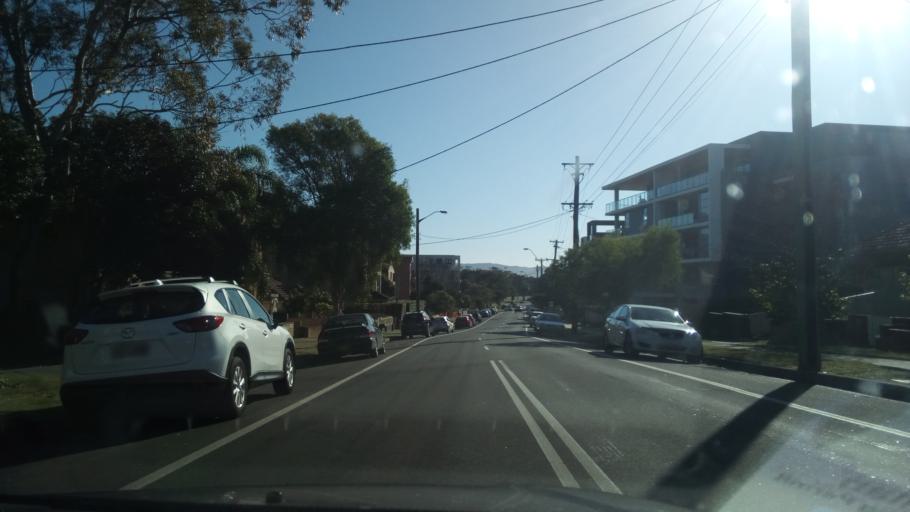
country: AU
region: New South Wales
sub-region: Wollongong
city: Gwynneville
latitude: -34.4137
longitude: 150.8958
